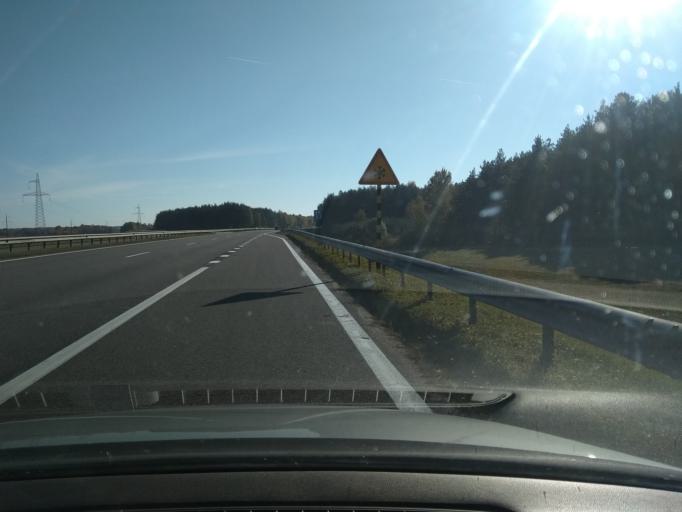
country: BY
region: Brest
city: Baranovichi
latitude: 53.0880
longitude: 25.8869
